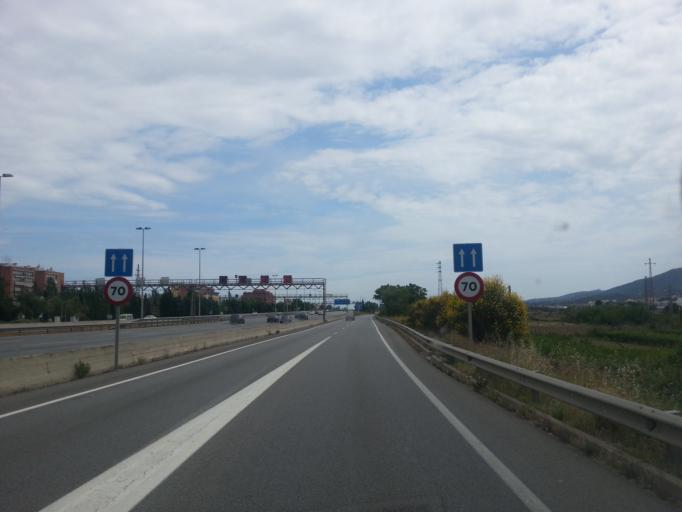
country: ES
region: Catalonia
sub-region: Provincia de Barcelona
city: Molins de Rei
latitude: 41.4182
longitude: 2.0089
